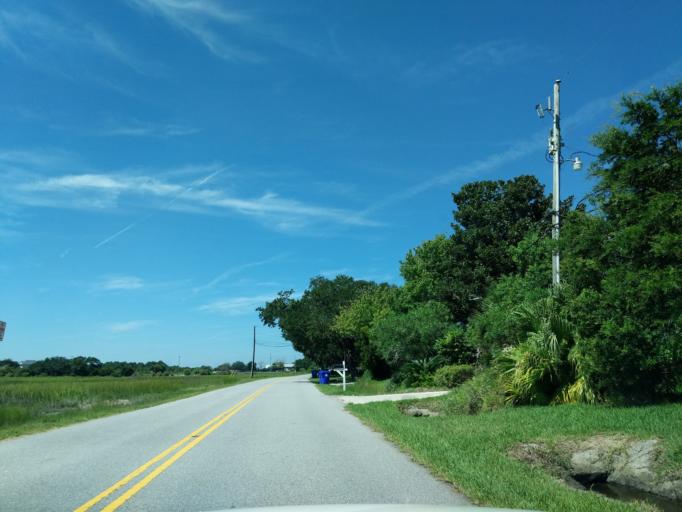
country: US
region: South Carolina
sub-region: Charleston County
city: Folly Beach
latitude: 32.6931
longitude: -79.9606
